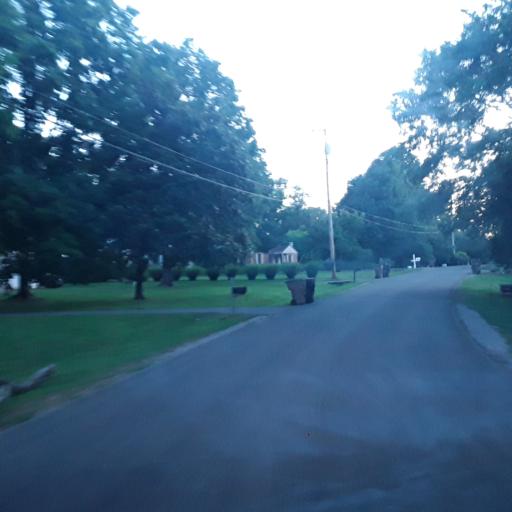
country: US
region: Tennessee
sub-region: Davidson County
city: Oak Hill
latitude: 36.0690
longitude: -86.7662
